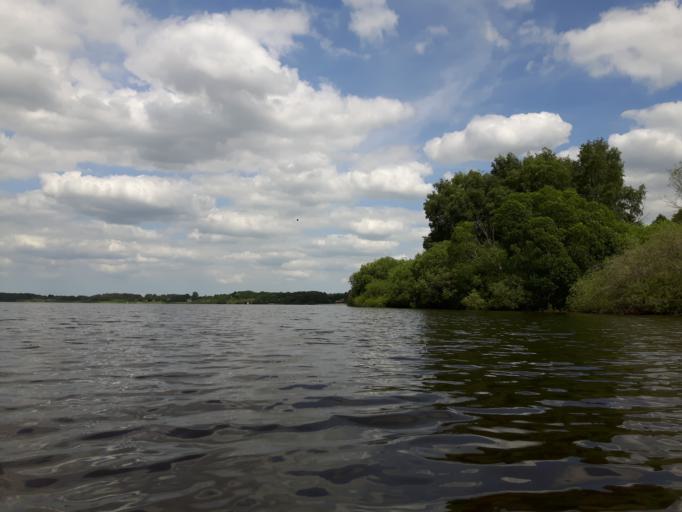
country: DE
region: Schleswig-Holstein
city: Muhbrook
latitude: 54.1341
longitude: 9.9962
